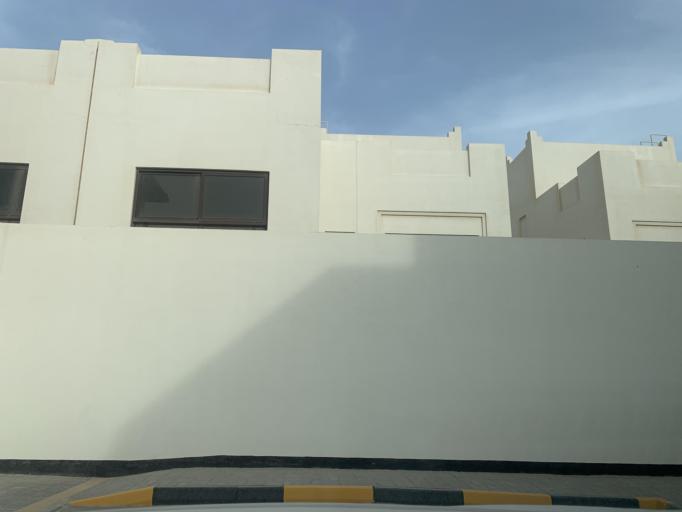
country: BH
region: Muharraq
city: Al Muharraq
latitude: 26.3153
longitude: 50.6207
